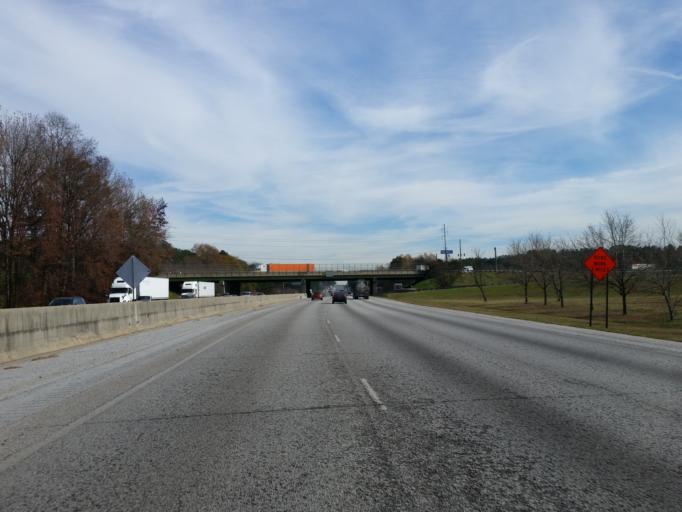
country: US
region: Georgia
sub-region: Cobb County
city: Austell
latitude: 33.7770
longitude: -84.6084
